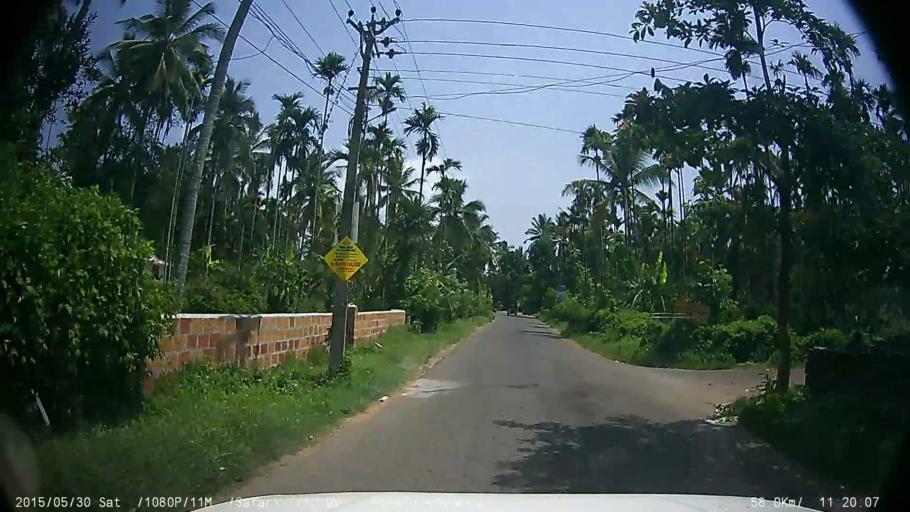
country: IN
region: Kerala
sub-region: Wayanad
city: Panamaram
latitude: 11.7929
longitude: 76.0411
